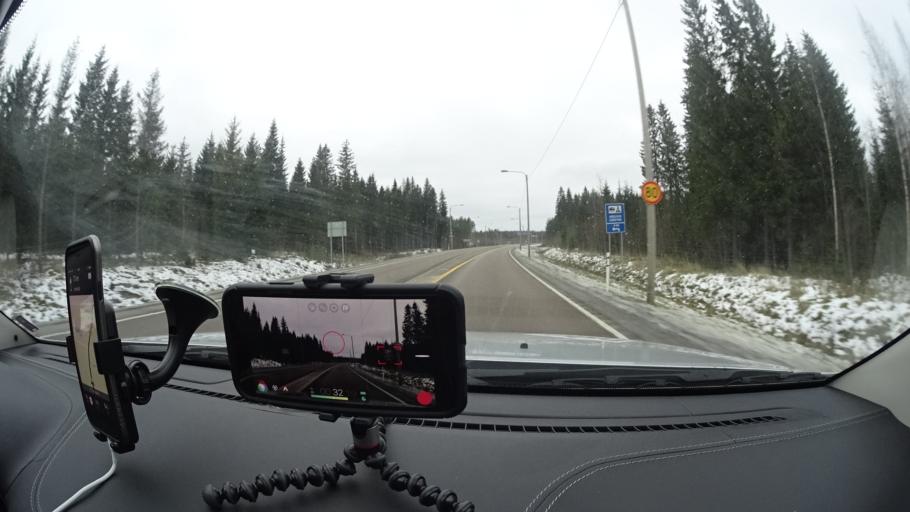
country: FI
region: Paijanne Tavastia
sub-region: Lahti
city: Hartola
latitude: 61.4436
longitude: 25.9912
